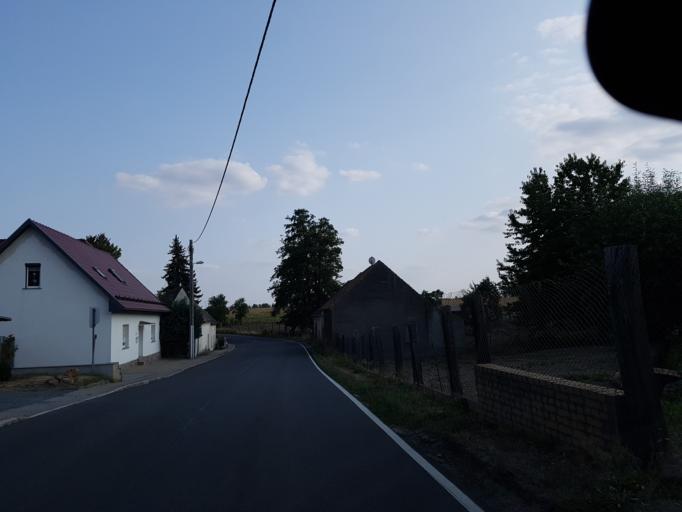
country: DE
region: Saxony
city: Dommitzsch
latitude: 51.6560
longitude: 12.8595
